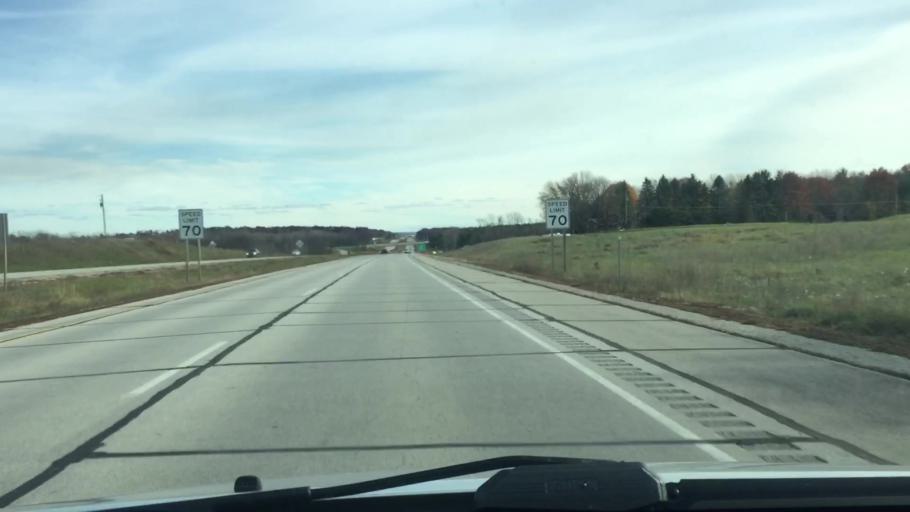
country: US
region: Wisconsin
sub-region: Brown County
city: Howard
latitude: 44.5650
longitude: -88.1420
